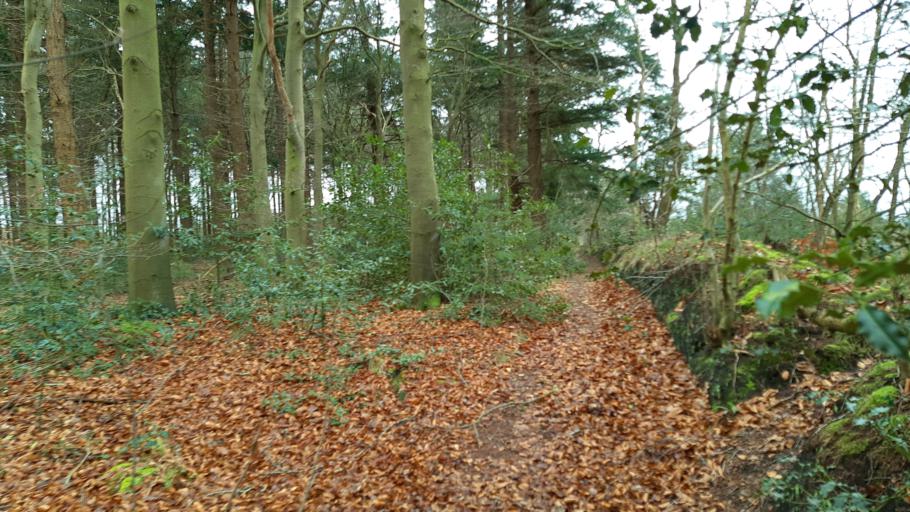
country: NL
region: Drenthe
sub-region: Gemeente Assen
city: Assen
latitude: 52.8524
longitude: 6.5867
